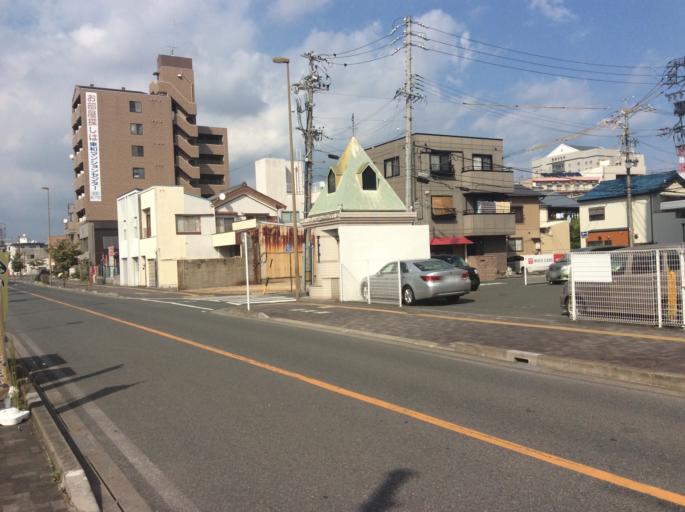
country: JP
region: Aichi
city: Toyohashi
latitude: 34.7674
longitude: 137.3881
